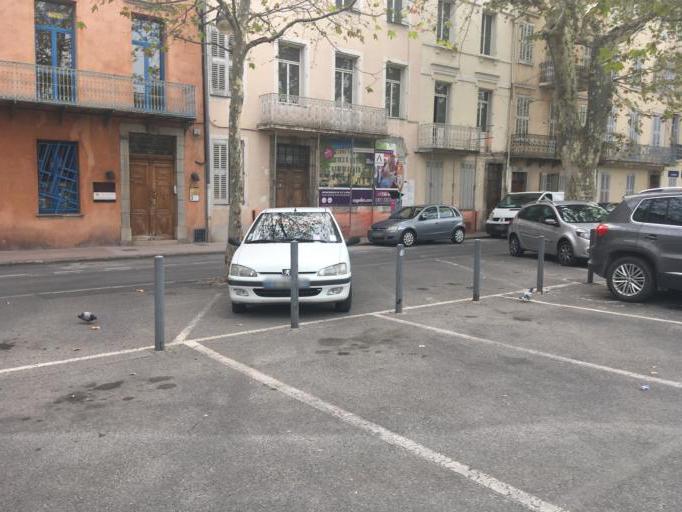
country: FR
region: Provence-Alpes-Cote d'Azur
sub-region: Departement du Var
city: Draguignan
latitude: 43.5366
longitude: 6.4613
